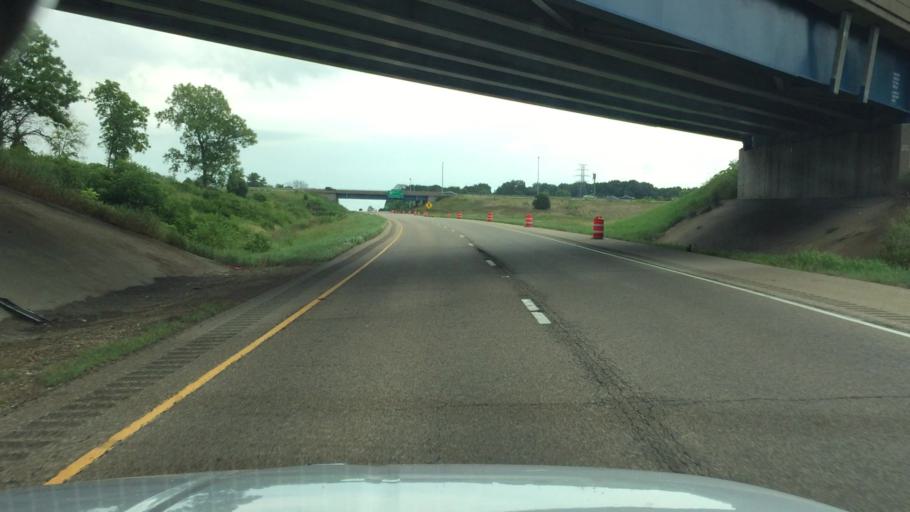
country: US
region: Illinois
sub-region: Peoria County
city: Bellevue
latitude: 40.7421
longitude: -89.6718
